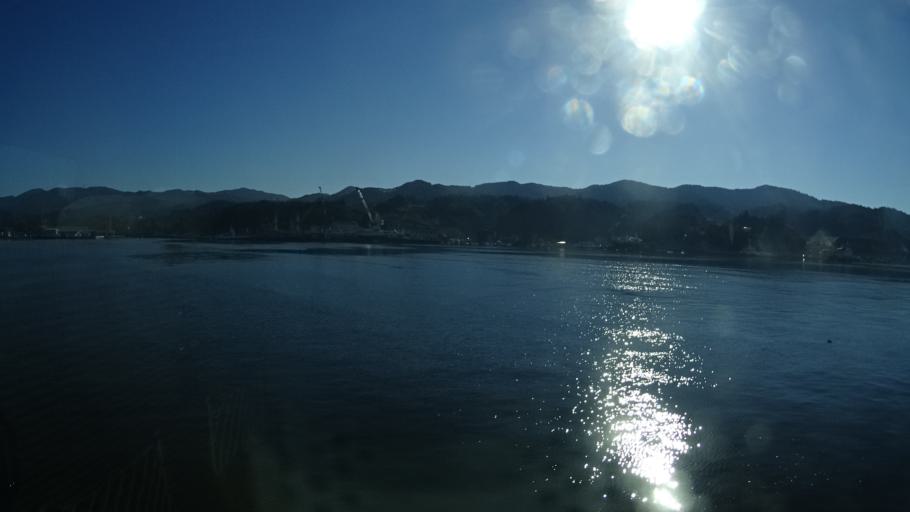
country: JP
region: Iwate
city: Ofunato
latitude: 38.9039
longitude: 141.5818
